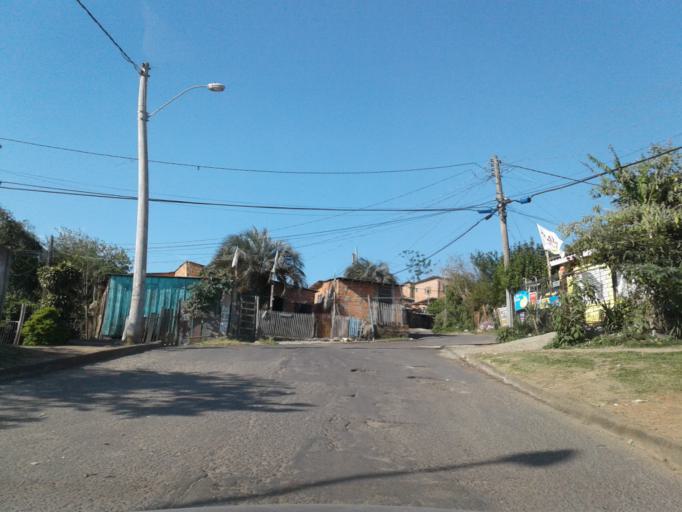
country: BR
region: Rio Grande do Sul
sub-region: Porto Alegre
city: Porto Alegre
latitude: -30.0479
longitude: -51.1551
